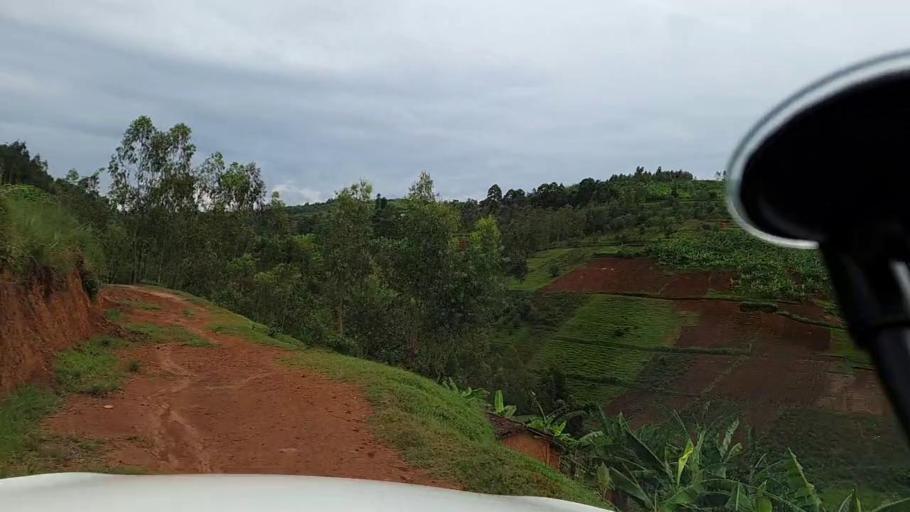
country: RW
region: Southern Province
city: Gitarama
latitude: -2.0815
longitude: 29.6441
